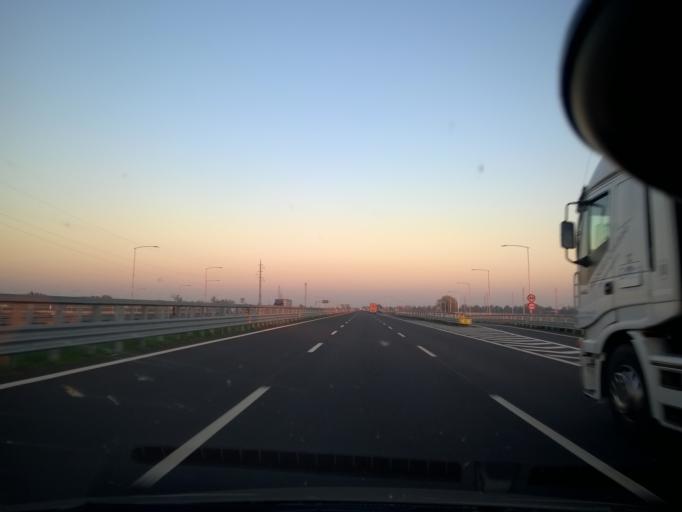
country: IT
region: Lombardy
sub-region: Provincia di Bergamo
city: Calcio
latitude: 45.4953
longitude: 9.8298
